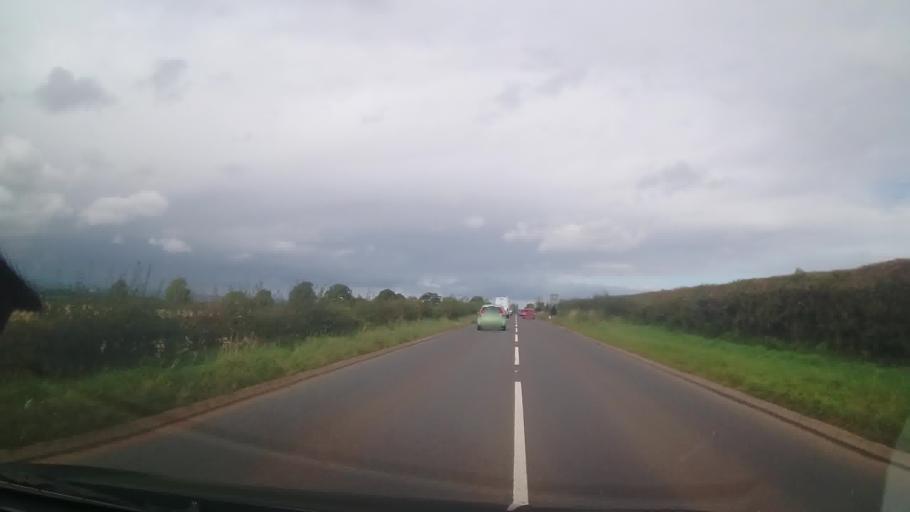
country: GB
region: England
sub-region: Shropshire
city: Alveley
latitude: 52.4796
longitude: -2.3540
